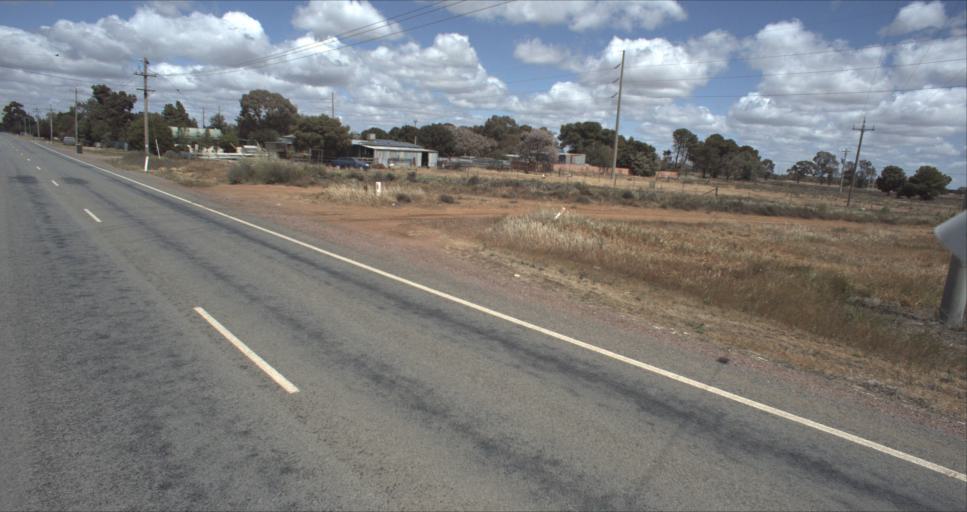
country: AU
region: New South Wales
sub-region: Murrumbidgee Shire
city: Darlington Point
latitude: -34.5098
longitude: 146.1865
